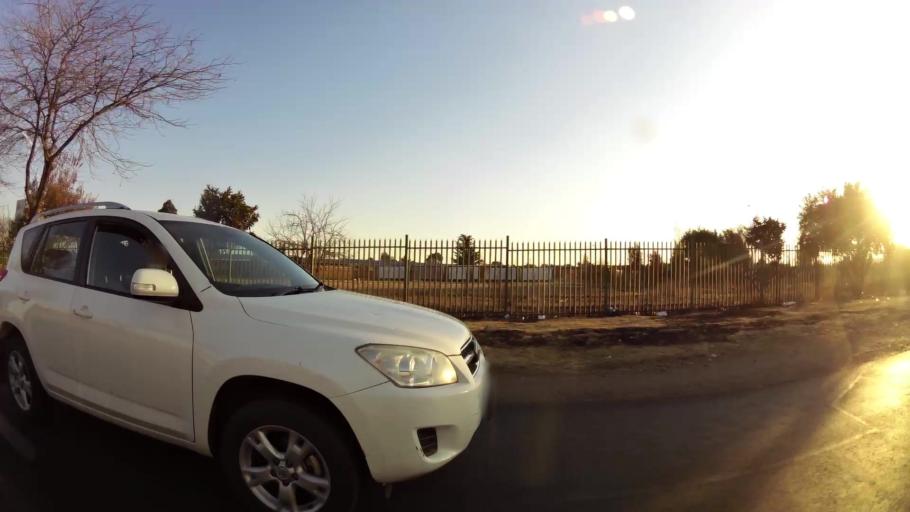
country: ZA
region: Gauteng
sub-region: City of Johannesburg Metropolitan Municipality
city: Soweto
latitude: -26.2416
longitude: 27.8799
